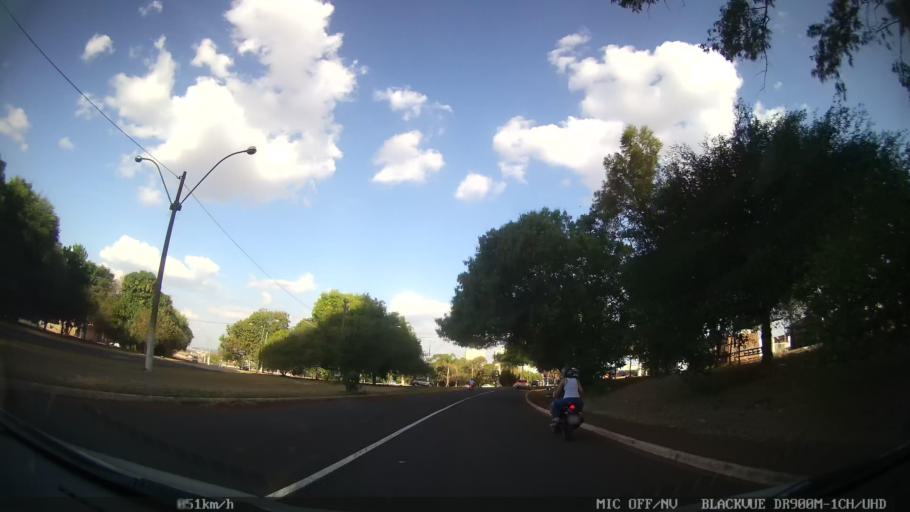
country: BR
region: Sao Paulo
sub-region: Ribeirao Preto
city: Ribeirao Preto
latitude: -21.1308
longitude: -47.8414
